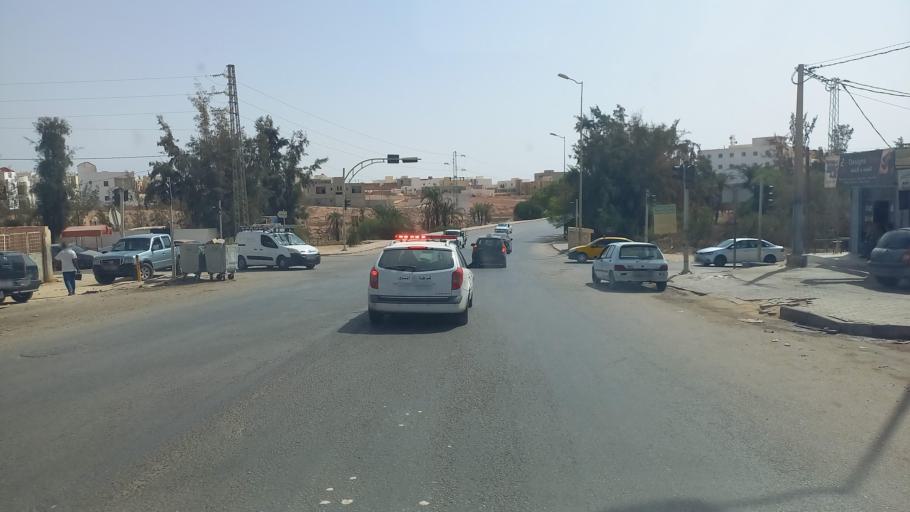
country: TN
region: Madanin
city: Medenine
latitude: 33.3446
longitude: 10.4991
